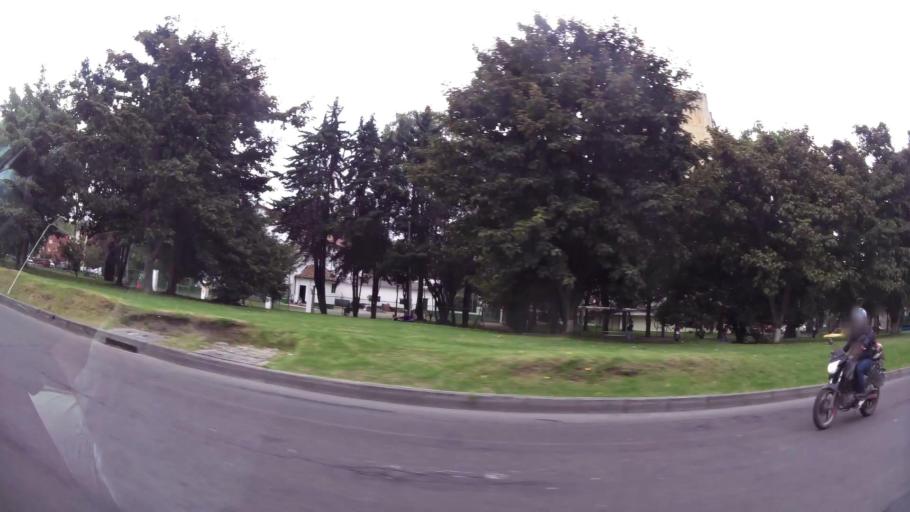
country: CO
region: Bogota D.C.
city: Bogota
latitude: 4.6255
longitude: -74.0877
